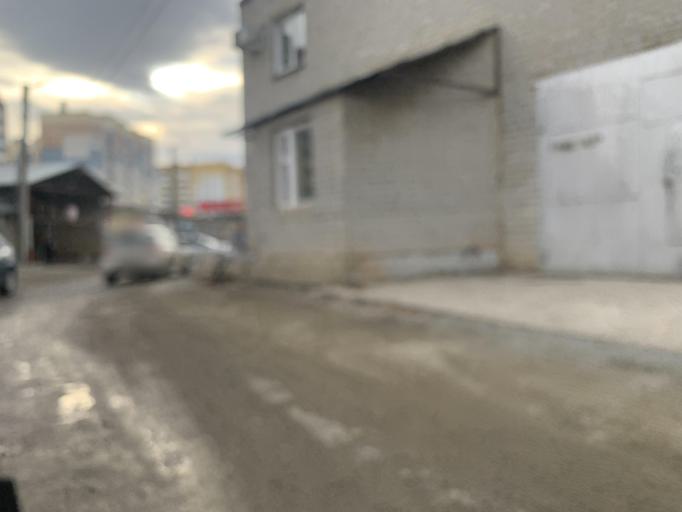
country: RU
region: Chelyabinsk
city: Roshchino
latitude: 55.1933
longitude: 61.2769
